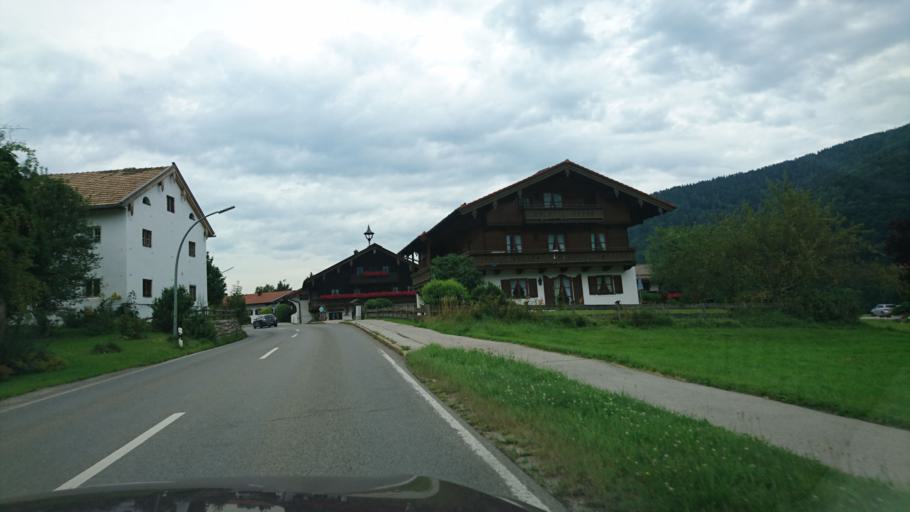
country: DE
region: Bavaria
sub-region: Upper Bavaria
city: Ruhpolding
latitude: 47.7540
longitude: 12.6551
